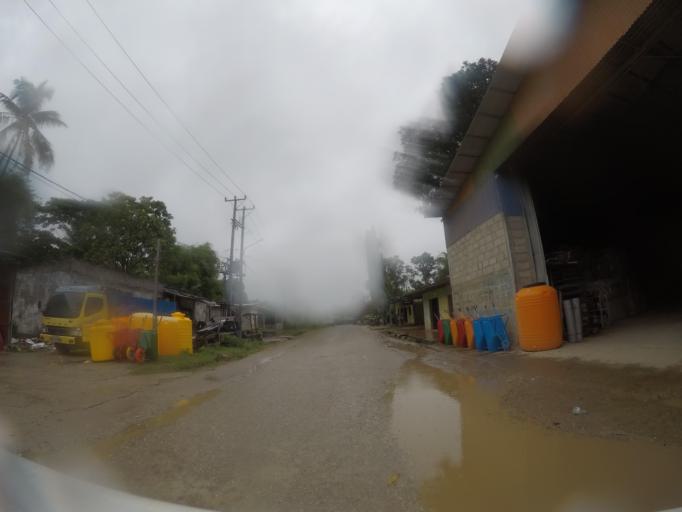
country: TL
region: Lautem
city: Lospalos
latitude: -8.5191
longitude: 126.9991
